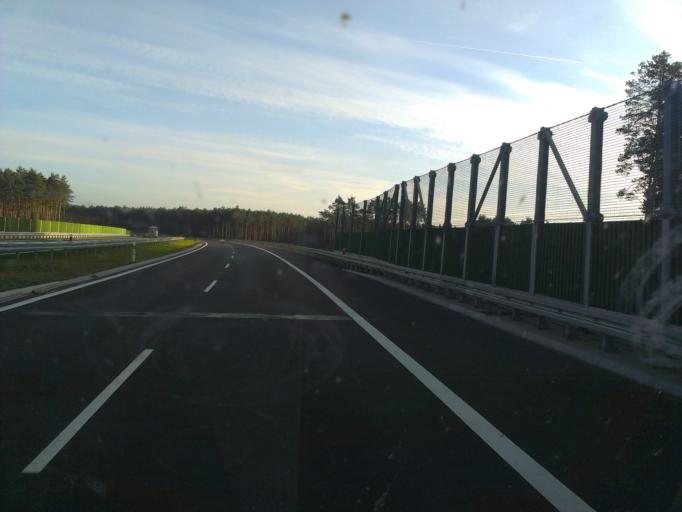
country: PL
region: Lubusz
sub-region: Powiat miedzyrzecki
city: Skwierzyna
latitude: 52.5611
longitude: 15.4752
